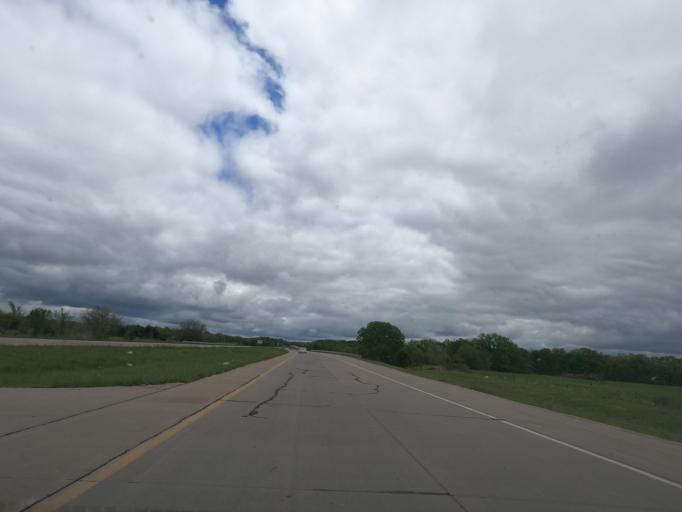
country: US
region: Kansas
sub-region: Wilson County
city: Neodesha
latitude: 37.3574
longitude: -95.6888
